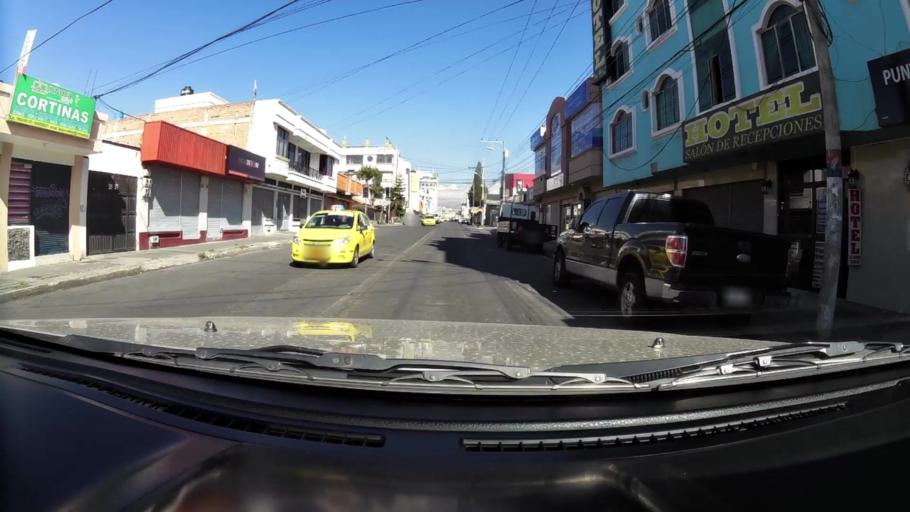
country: EC
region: Chimborazo
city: Riobamba
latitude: -1.6642
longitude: -78.6575
